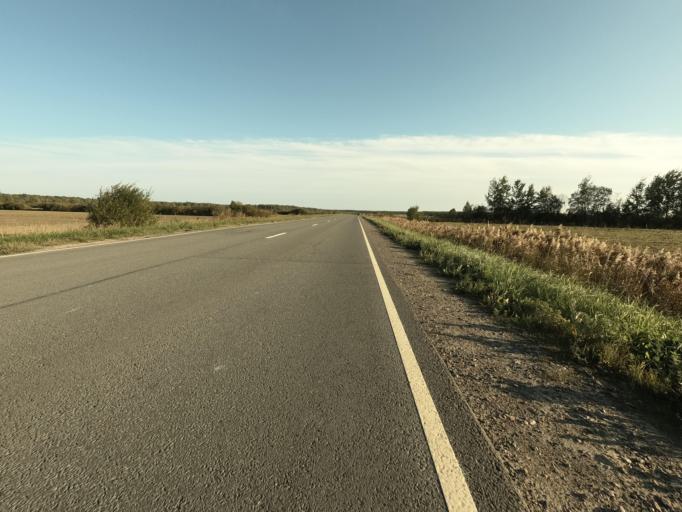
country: RU
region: St.-Petersburg
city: Sapernyy
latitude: 59.7437
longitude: 30.6474
